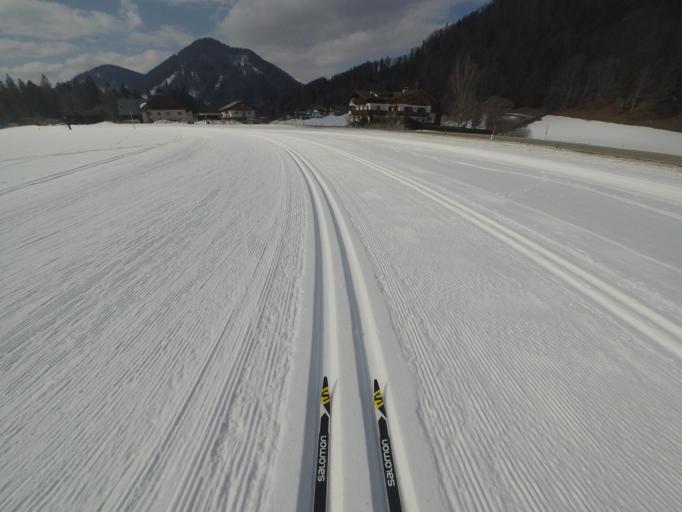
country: AT
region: Salzburg
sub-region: Politischer Bezirk Salzburg-Umgebung
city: Fuschl am See
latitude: 47.7723
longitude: 13.3100
